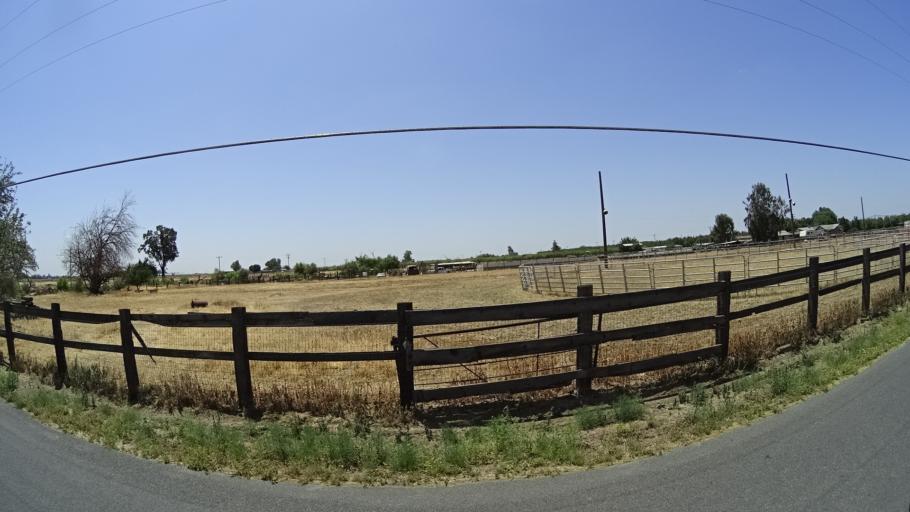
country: US
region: California
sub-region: Kings County
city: Armona
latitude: 36.3058
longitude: -119.7073
